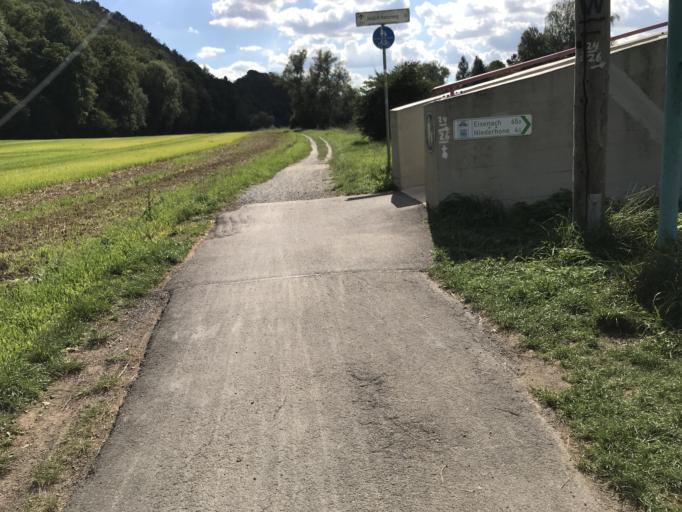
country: DE
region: Hesse
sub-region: Regierungsbezirk Kassel
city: Bad Sooden-Allendorf
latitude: 51.2294
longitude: 9.9997
